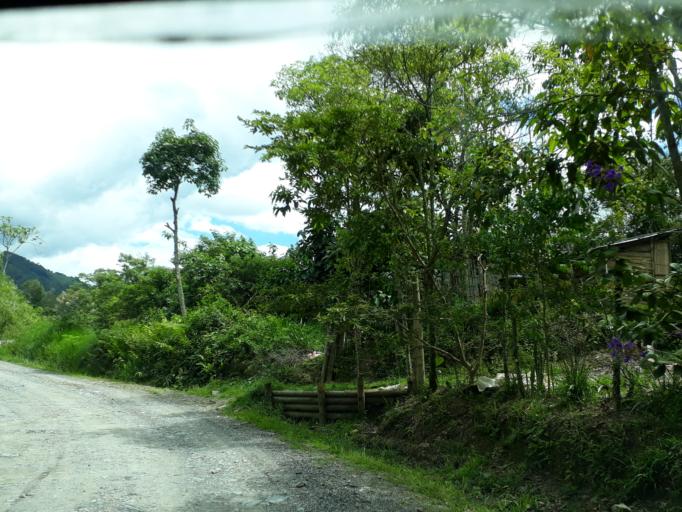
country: CO
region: Cundinamarca
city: Topaipi
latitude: 5.3412
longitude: -74.1874
